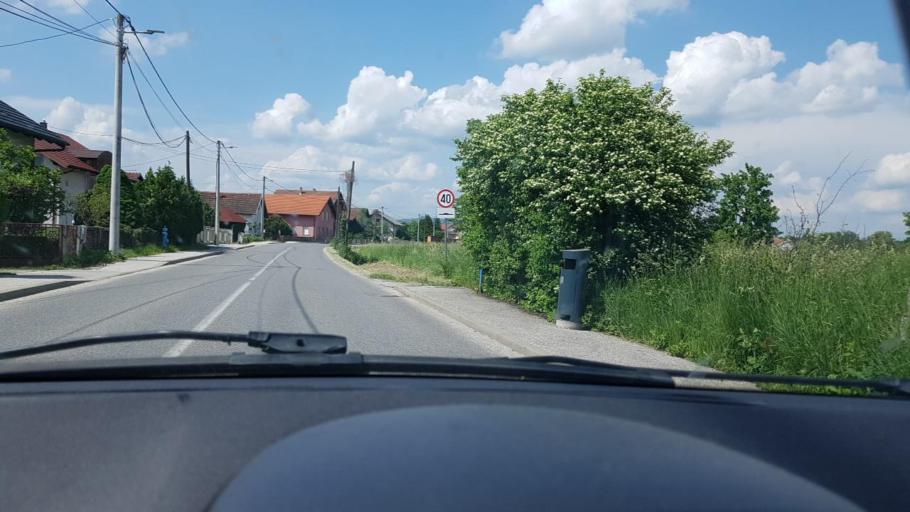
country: HR
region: Grad Zagreb
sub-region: Sesvete
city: Sesvete
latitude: 45.8820
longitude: 16.1736
